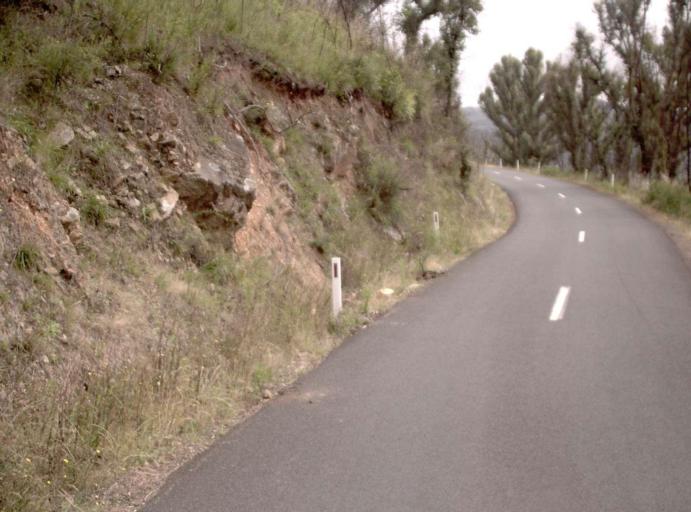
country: AU
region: Victoria
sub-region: Wellington
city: Heyfield
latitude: -37.7313
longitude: 146.6697
